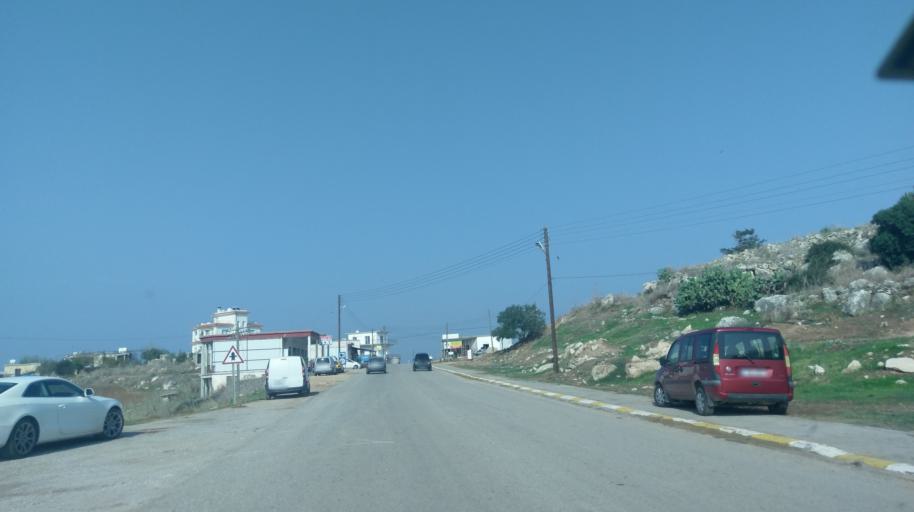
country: CY
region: Ammochostos
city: Leonarisso
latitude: 35.5070
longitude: 34.1607
